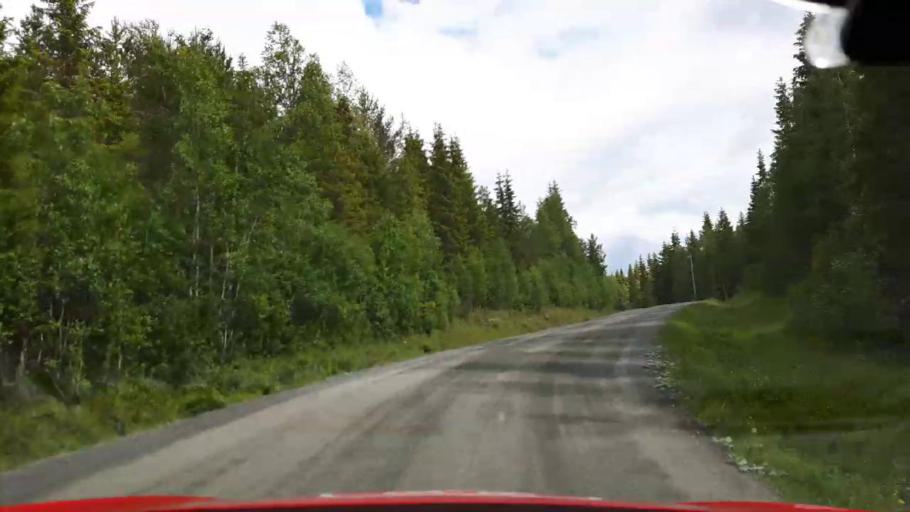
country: NO
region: Nord-Trondelag
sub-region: Lierne
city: Sandvika
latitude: 64.1458
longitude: 13.9013
